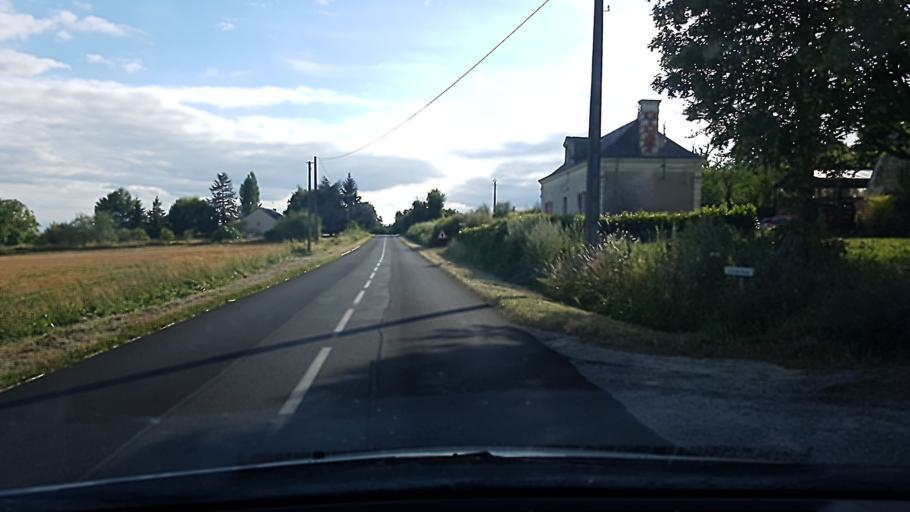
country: FR
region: Pays de la Loire
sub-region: Departement de Maine-et-Loire
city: Maze
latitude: 47.4979
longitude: -0.2637
